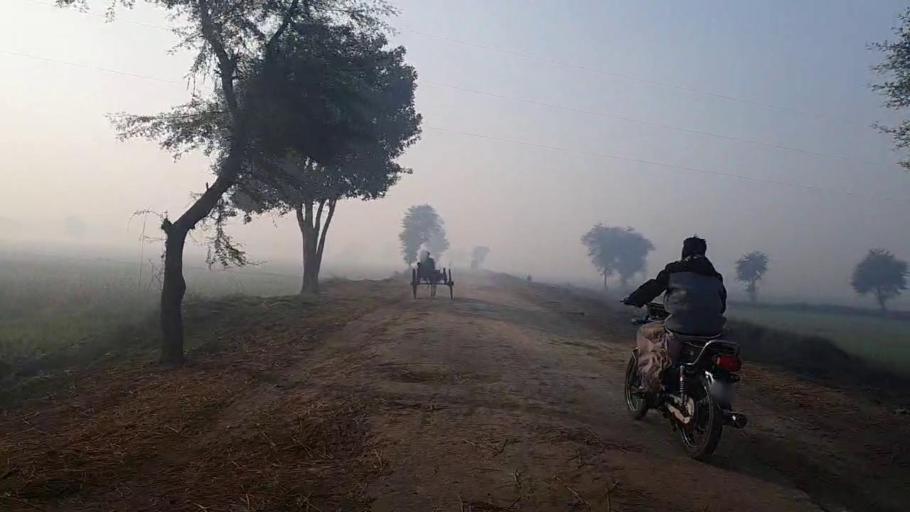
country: PK
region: Sindh
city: Mehar
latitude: 27.1578
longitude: 67.8240
